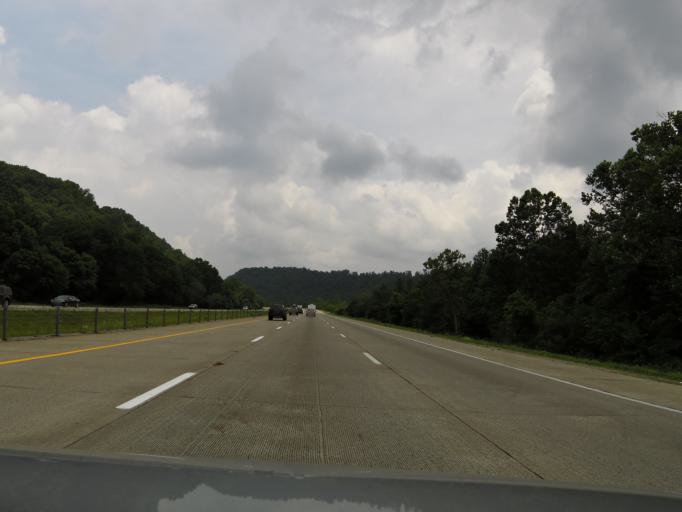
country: US
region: Kentucky
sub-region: Bullitt County
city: Lebanon Junction
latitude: 37.7751
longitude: -85.7786
